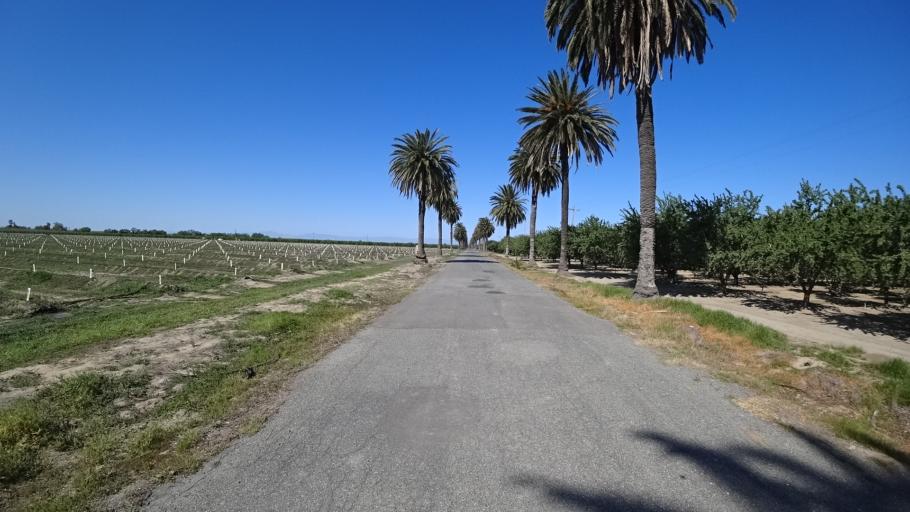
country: US
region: California
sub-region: Glenn County
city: Hamilton City
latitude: 39.7374
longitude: -122.0230
